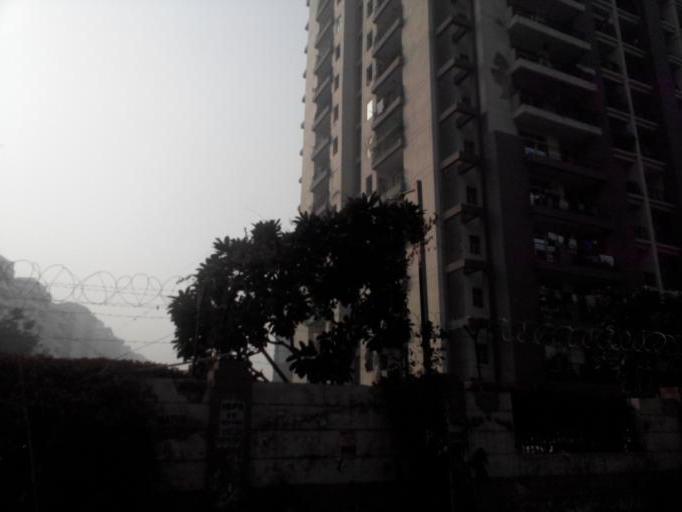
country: IN
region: Uttar Pradesh
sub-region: Gautam Buddha Nagar
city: Noida
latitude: 28.6376
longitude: 77.3659
